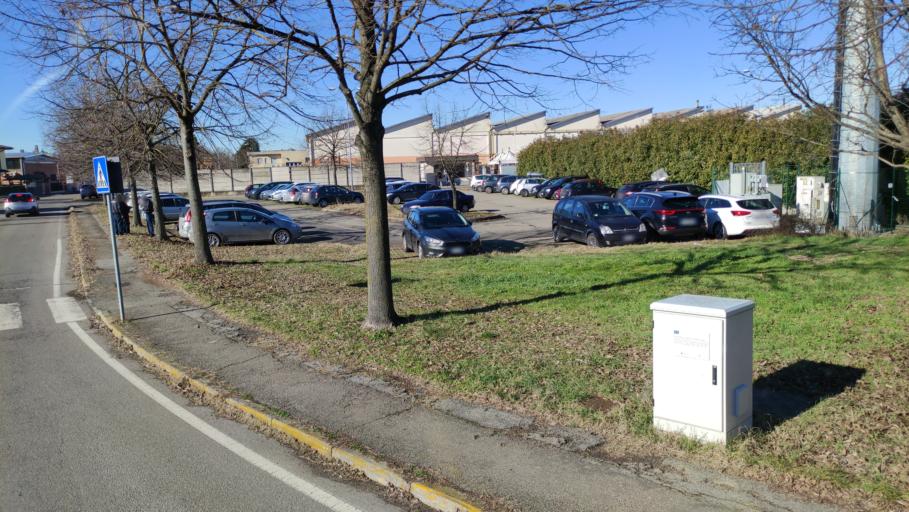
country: IT
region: Emilia-Romagna
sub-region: Provincia di Reggio Emilia
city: San Martino in Rio
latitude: 44.7321
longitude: 10.7792
